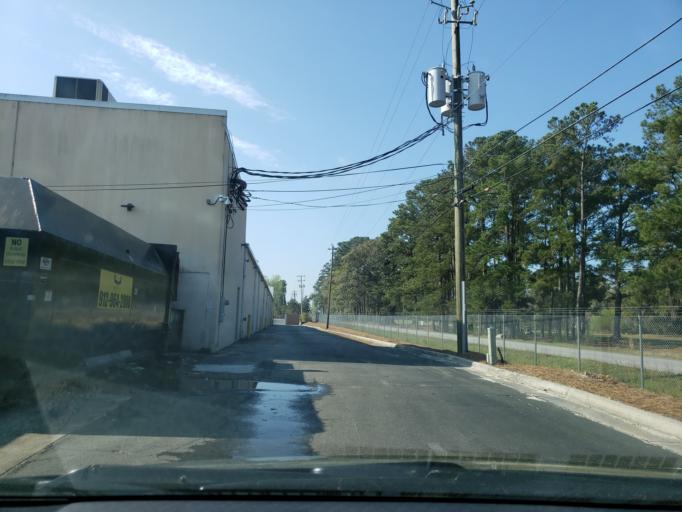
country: US
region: Georgia
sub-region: Chatham County
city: Montgomery
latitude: 32.0040
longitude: -81.1254
